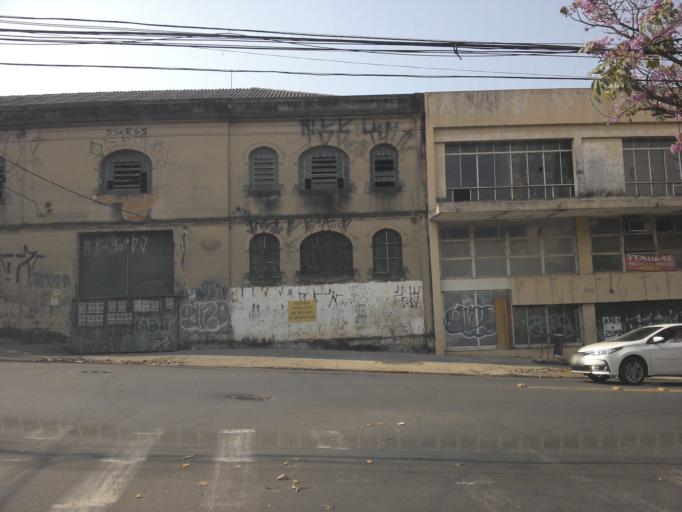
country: BR
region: Sao Paulo
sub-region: Campinas
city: Campinas
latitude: -22.9130
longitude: -47.0851
